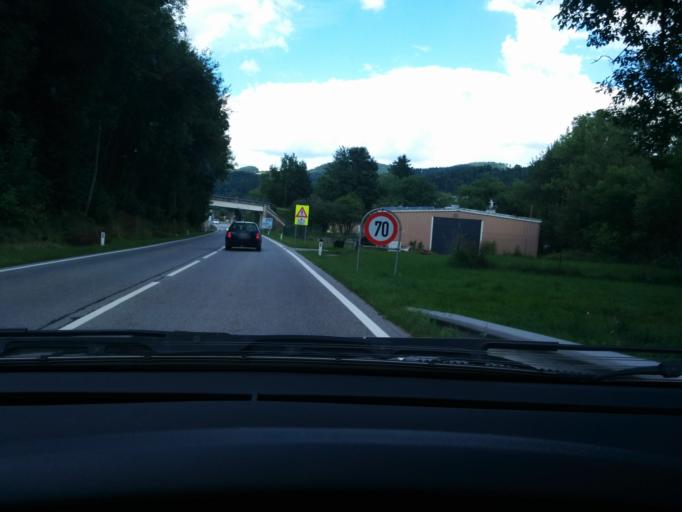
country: AT
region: Lower Austria
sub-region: Politischer Bezirk Neunkirchen
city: Thomasberg
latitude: 47.5570
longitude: 16.0900
